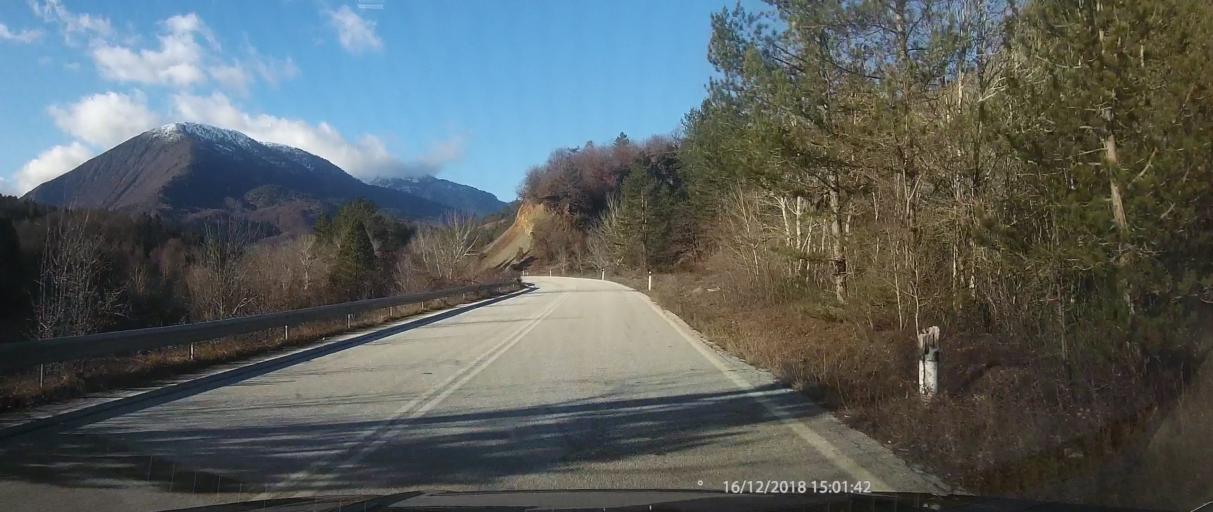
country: GR
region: West Macedonia
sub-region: Nomos Kastorias
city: Nestorio
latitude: 40.2235
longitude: 21.0036
